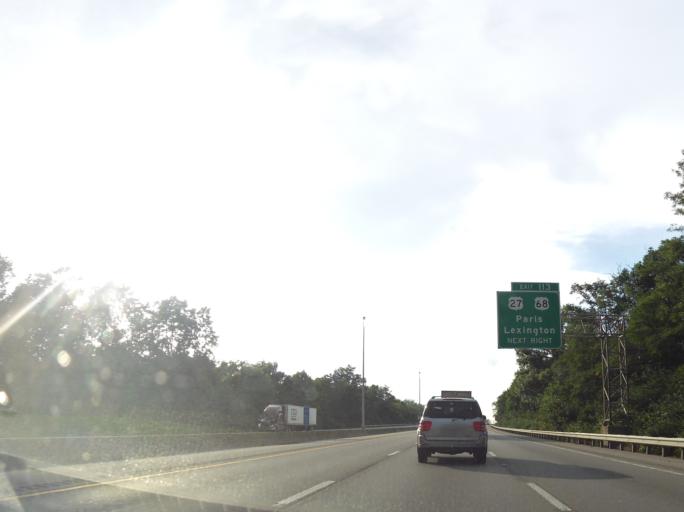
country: US
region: Kentucky
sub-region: Fayette County
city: Lexington-Fayette
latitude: 38.0719
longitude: -84.4519
